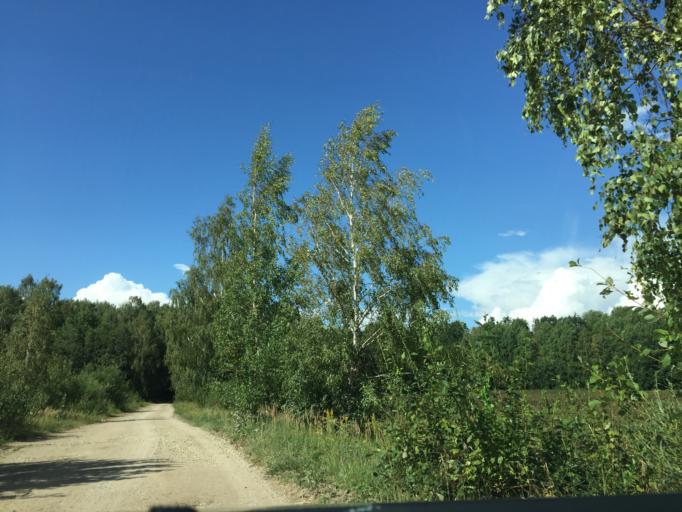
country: LT
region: Siauliu apskritis
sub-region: Joniskis
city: Joniskis
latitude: 56.3334
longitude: 23.5610
